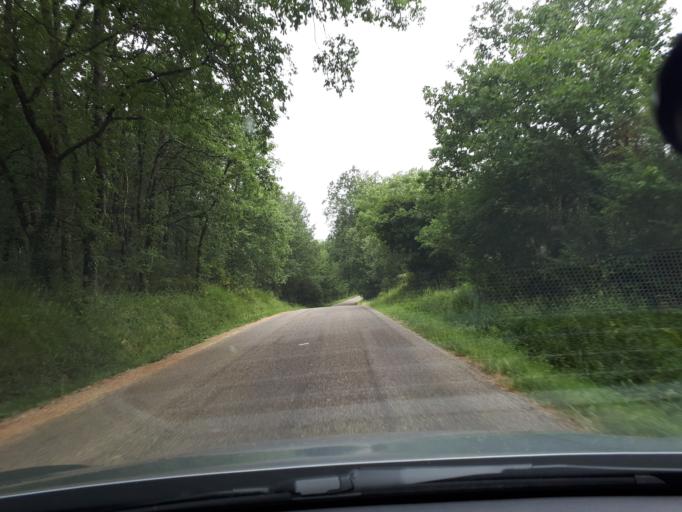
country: FR
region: Midi-Pyrenees
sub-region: Departement du Tarn-et-Garonne
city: Campsas
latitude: 43.8711
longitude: 1.3421
